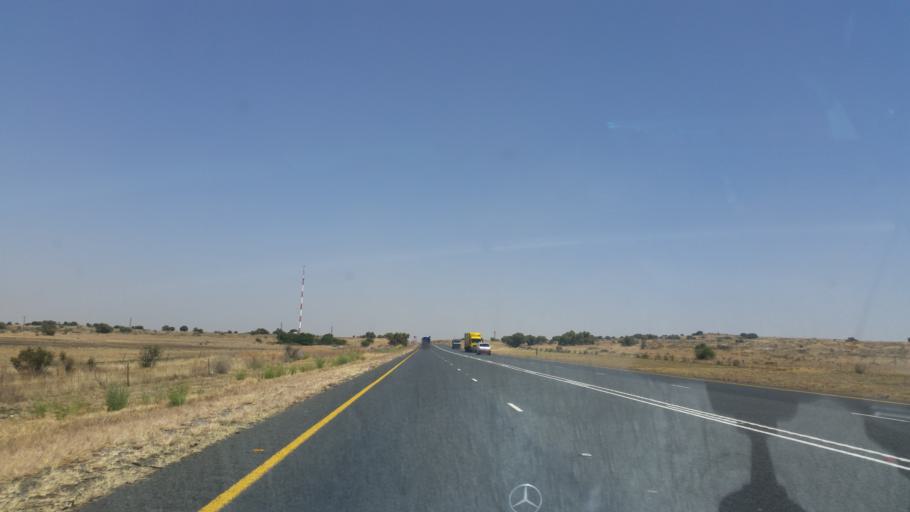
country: ZA
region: Orange Free State
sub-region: Lejweleputswa District Municipality
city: Winburg
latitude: -28.7118
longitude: 26.7820
